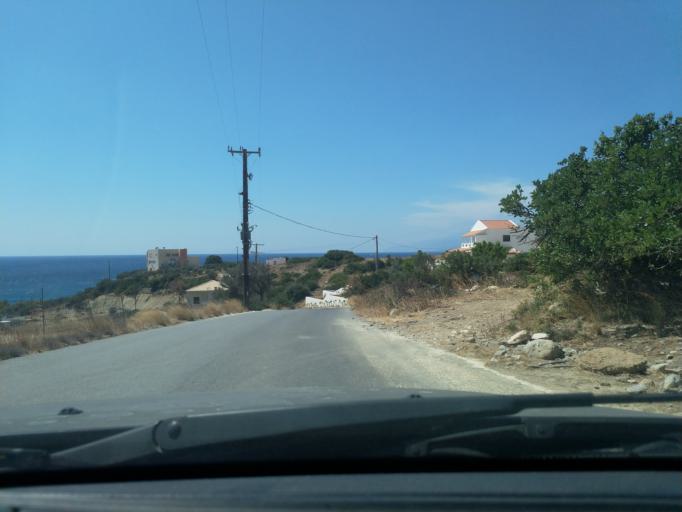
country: GR
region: Crete
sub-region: Nomos Rethymnis
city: Agia Galini
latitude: 35.1202
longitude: 24.5505
